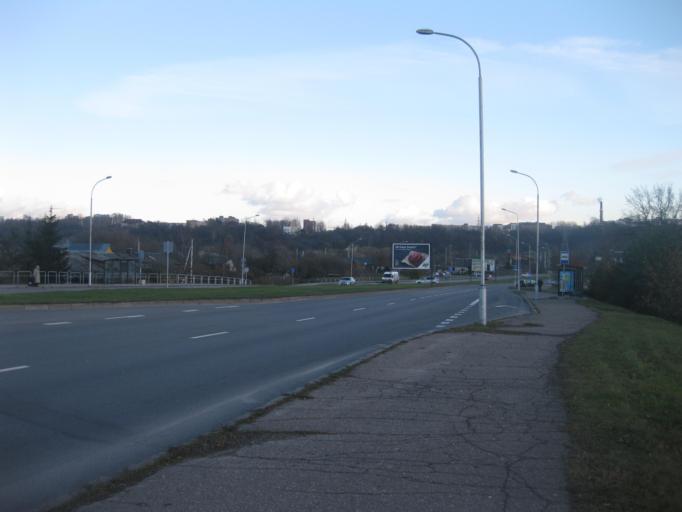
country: LT
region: Kauno apskritis
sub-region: Kaunas
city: Silainiai
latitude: 54.9253
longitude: 23.9050
